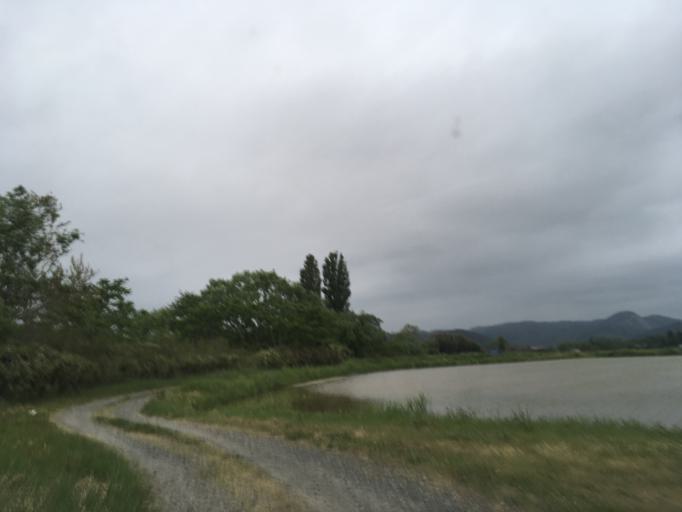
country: JP
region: Miyagi
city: Wakuya
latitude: 38.7142
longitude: 141.2849
